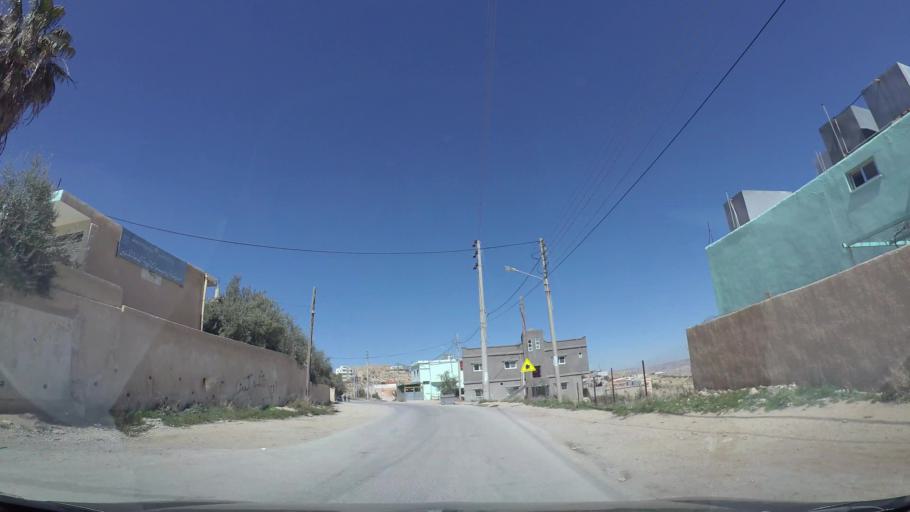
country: JO
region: Tafielah
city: At Tafilah
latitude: 30.8226
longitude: 35.5812
